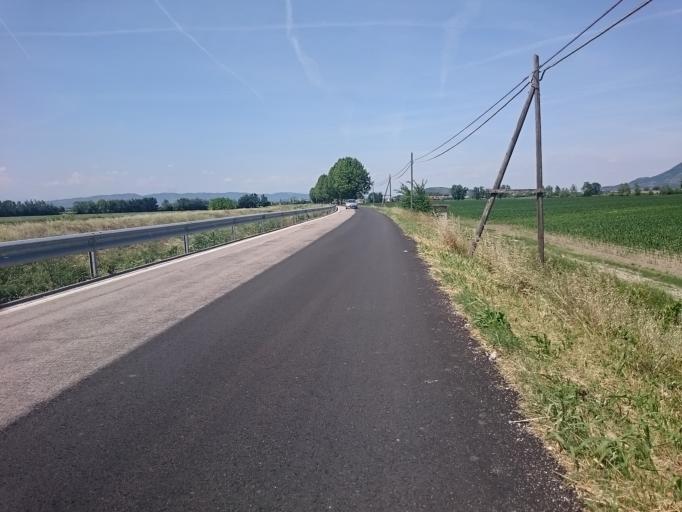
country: IT
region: Veneto
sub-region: Provincia di Padova
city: Lozzo Atestino
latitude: 45.3014
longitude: 11.6040
